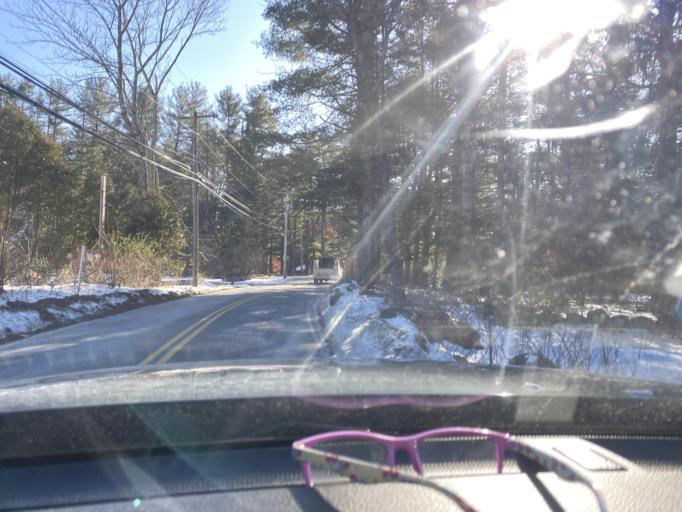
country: US
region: Massachusetts
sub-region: Norfolk County
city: Walpole
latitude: 42.1666
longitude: -71.2623
